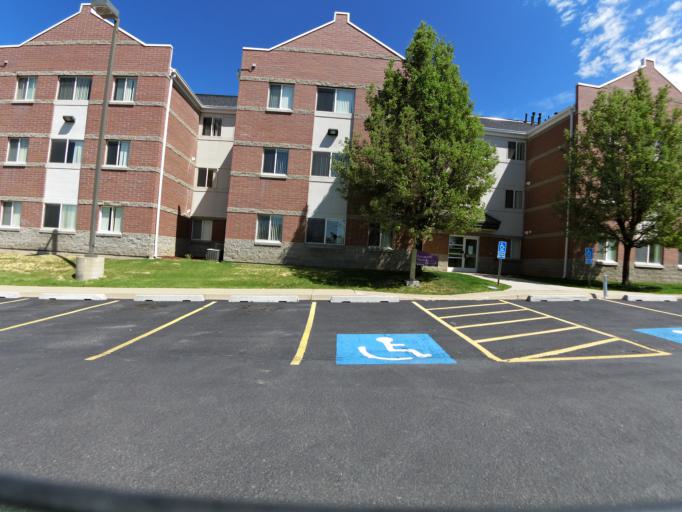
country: US
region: Utah
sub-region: Weber County
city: South Ogden
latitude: 41.1781
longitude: -111.9454
